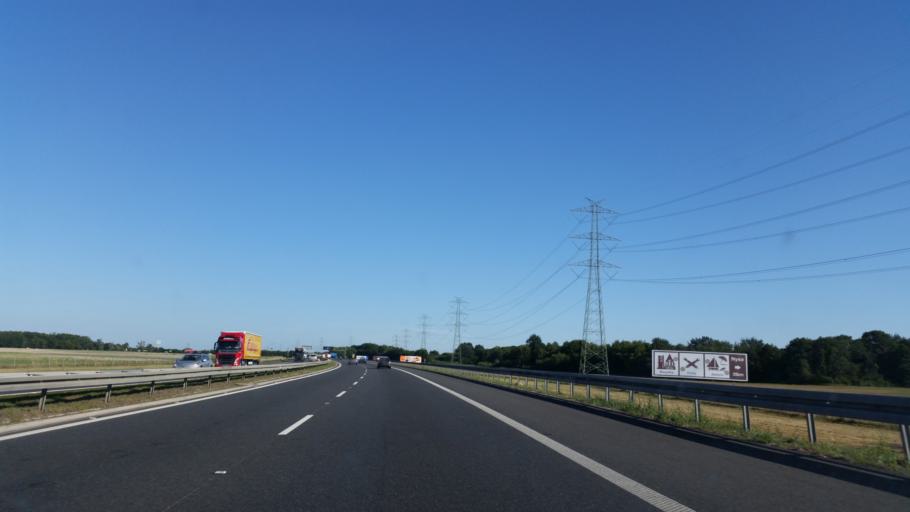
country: PL
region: Opole Voivodeship
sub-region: Powiat brzeski
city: Skarbimierz Osiedle
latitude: 50.7918
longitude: 17.3313
